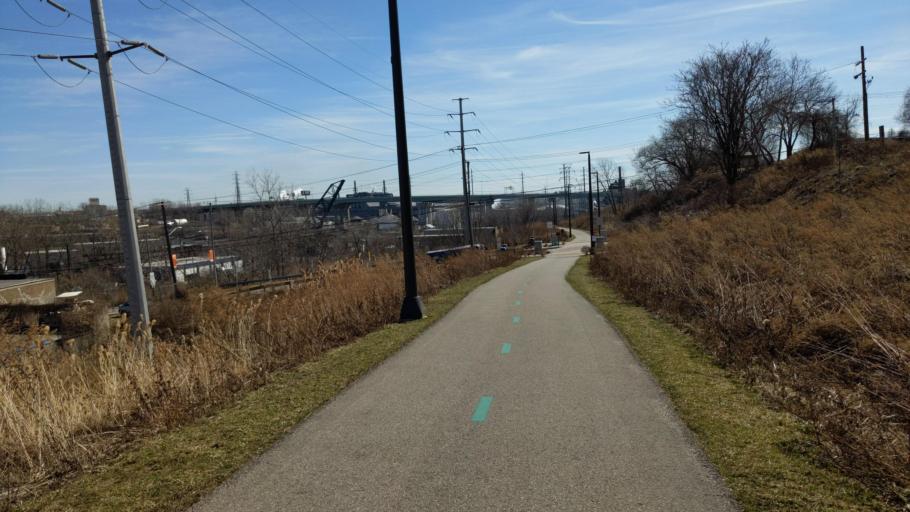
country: US
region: Ohio
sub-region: Cuyahoga County
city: Cleveland
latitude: 41.4824
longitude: -81.6812
